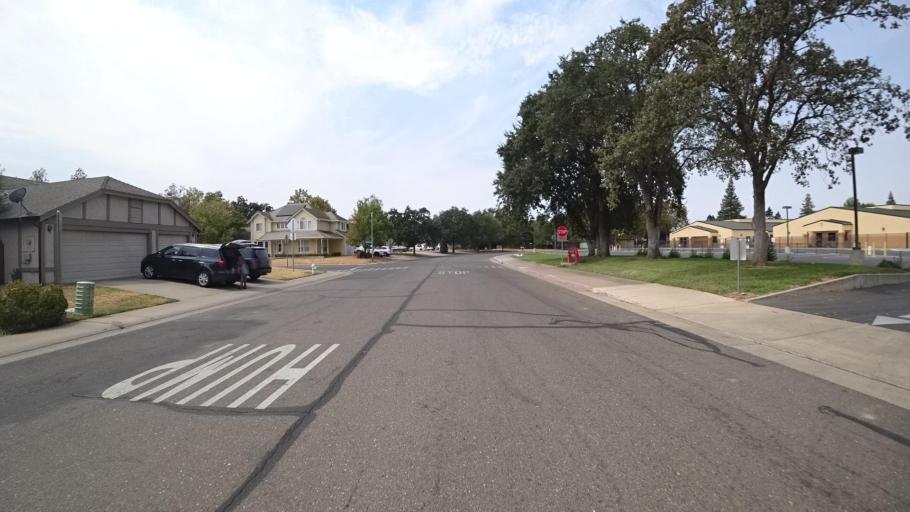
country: US
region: California
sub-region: Sacramento County
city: Elk Grove
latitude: 38.4166
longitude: -121.3861
